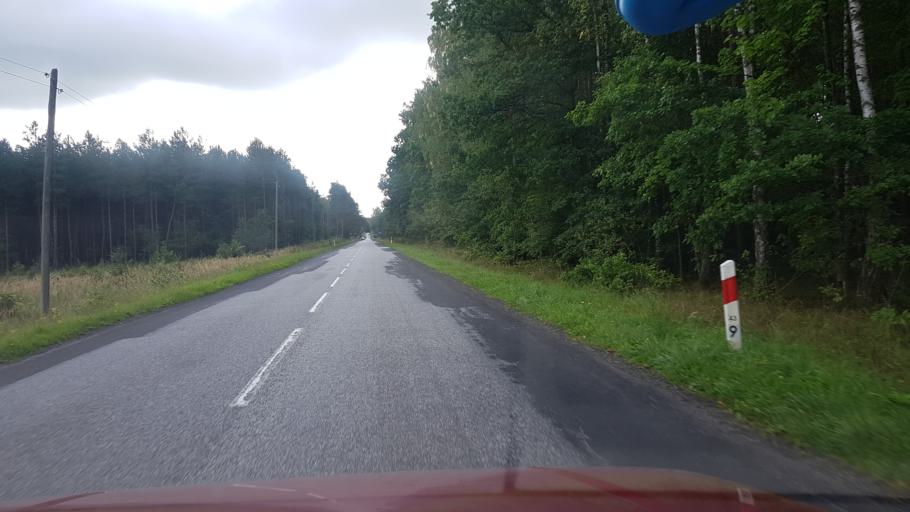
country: PL
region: West Pomeranian Voivodeship
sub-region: Powiat koszalinski
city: Polanow
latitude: 54.0993
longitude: 16.8158
